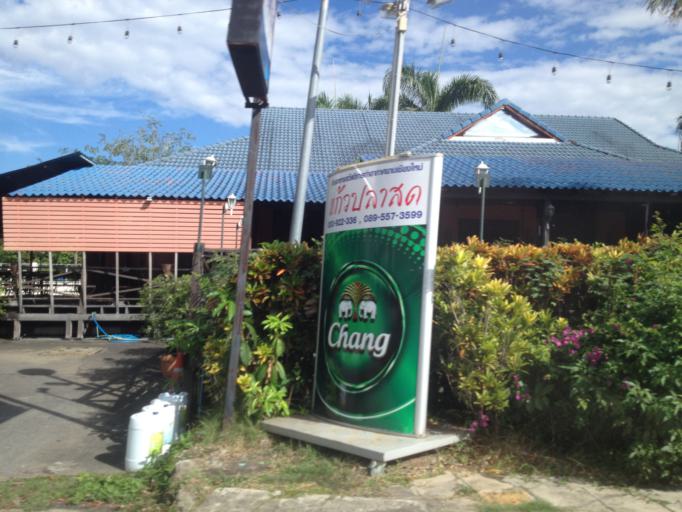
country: TH
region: Chiang Mai
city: Chiang Mai
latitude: 18.7676
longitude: 98.9690
